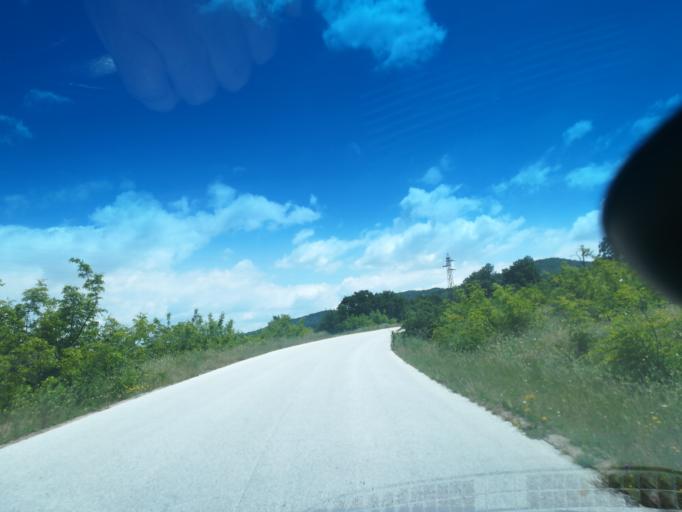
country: BG
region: Khaskovo
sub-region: Obshtina Mineralni Bani
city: Mineralni Bani
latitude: 41.9774
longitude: 25.2558
